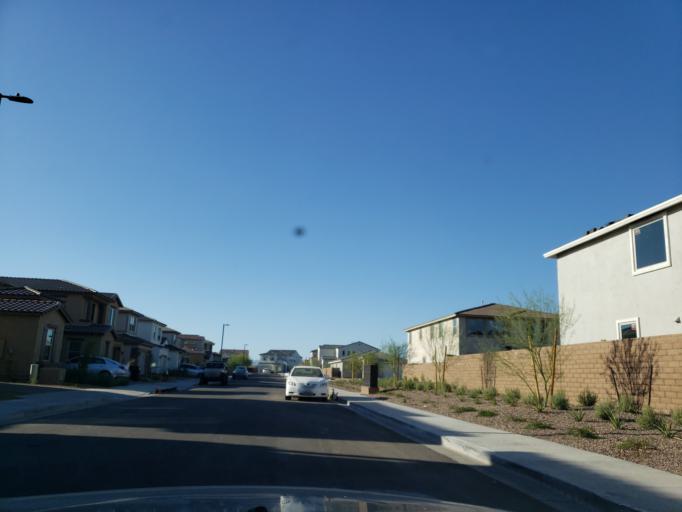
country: US
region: Arizona
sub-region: Maricopa County
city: Cave Creek
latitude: 33.6852
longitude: -112.0100
